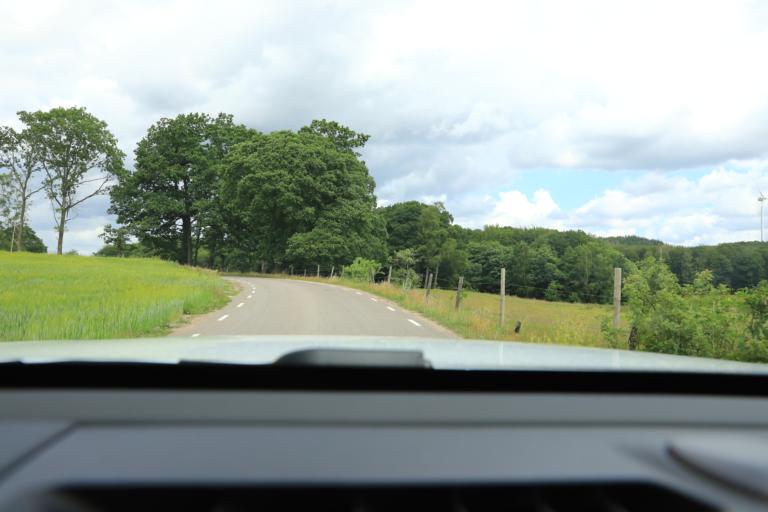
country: SE
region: Halland
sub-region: Varbergs Kommun
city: Tvaaker
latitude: 57.0398
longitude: 12.4706
